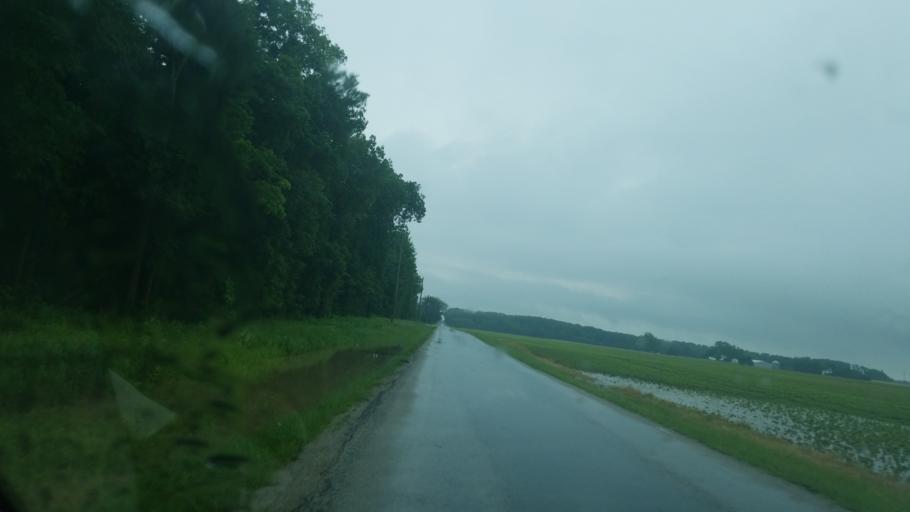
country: US
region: Ohio
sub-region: Huron County
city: Plymouth
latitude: 40.9449
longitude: -82.6958
